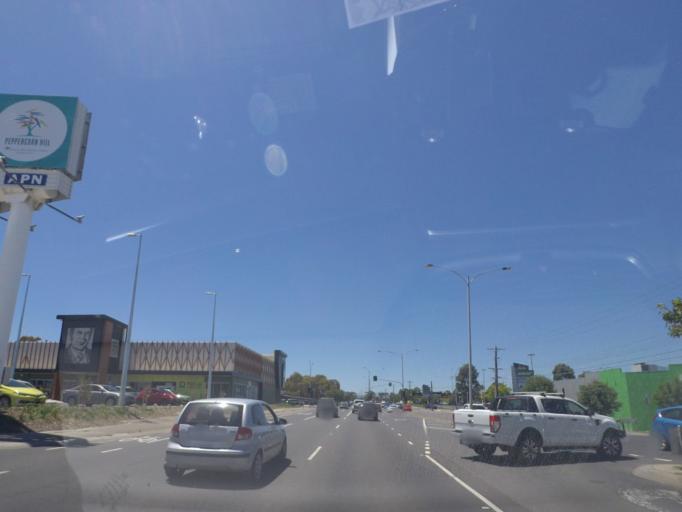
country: AU
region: Victoria
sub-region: Whittlesea
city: Lalor
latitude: -37.6559
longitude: 145.0209
